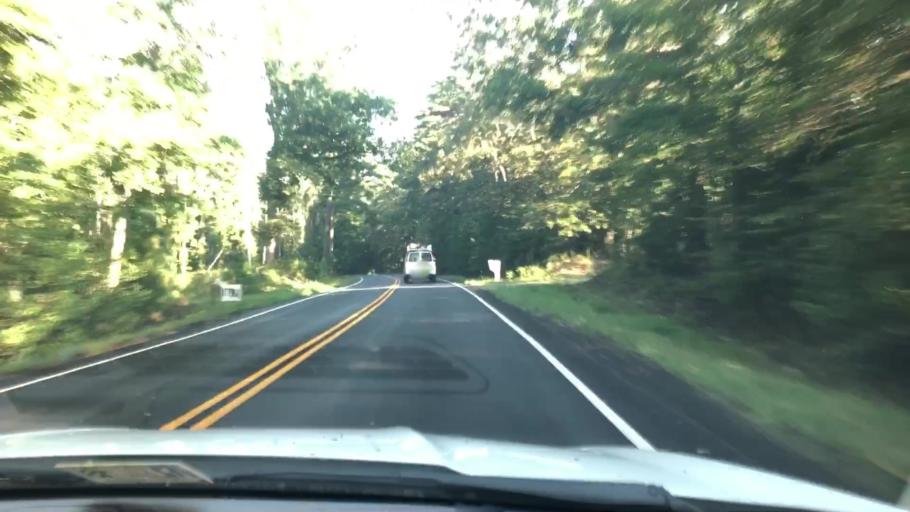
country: US
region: Virginia
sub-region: King William County
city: West Point
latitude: 37.4767
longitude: -76.8465
